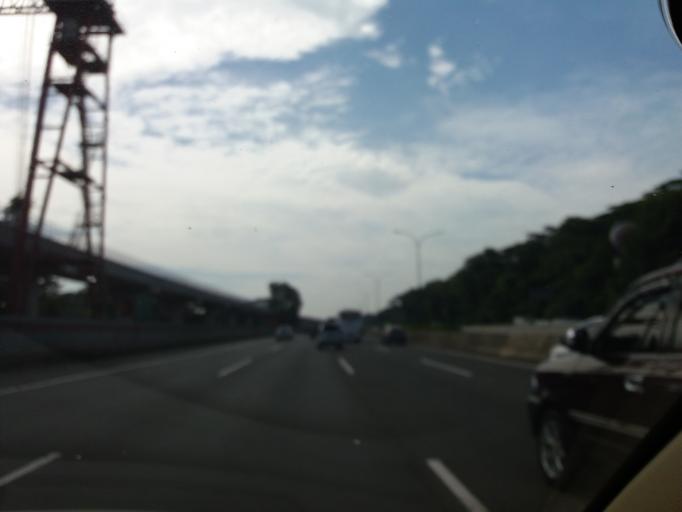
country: ID
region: West Java
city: Cileungsir
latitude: -6.3302
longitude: 106.8871
